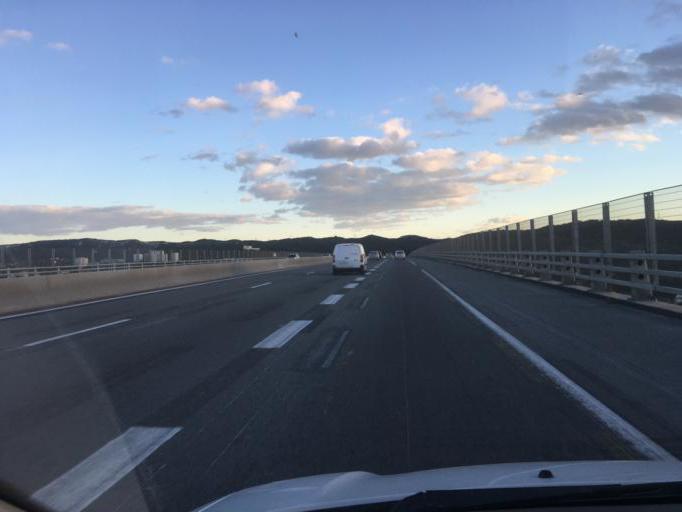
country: FR
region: Provence-Alpes-Cote d'Azur
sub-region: Departement des Bouches-du-Rhone
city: Martigues
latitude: 43.4033
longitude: 5.0415
